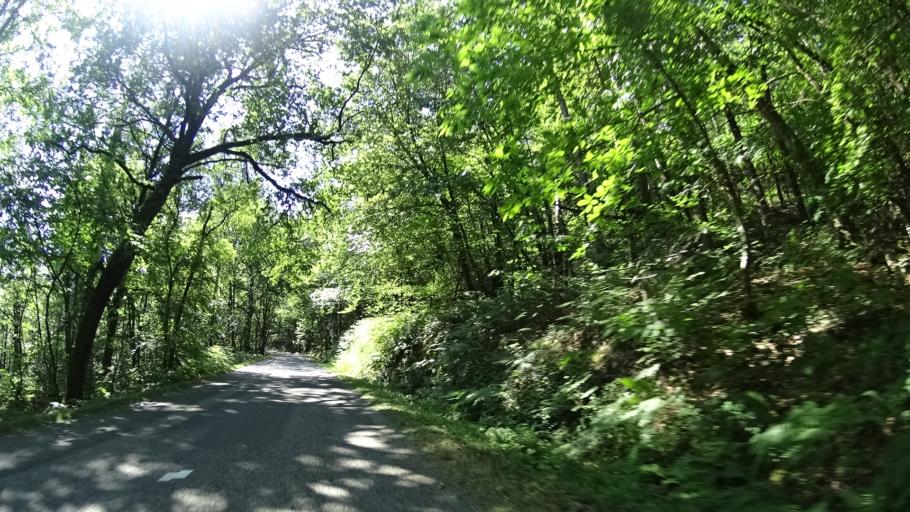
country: FR
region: Brittany
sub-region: Departement d'Ille-et-Vilaine
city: Langon
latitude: 47.7647
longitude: -1.8488
